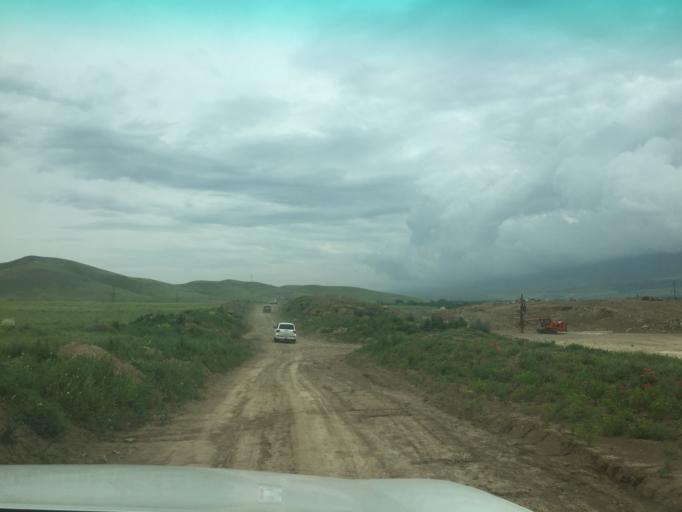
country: KZ
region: Ongtustik Qazaqstan
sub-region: Tulkibas Audany
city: Zhabagly
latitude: 42.5183
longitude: 70.5395
